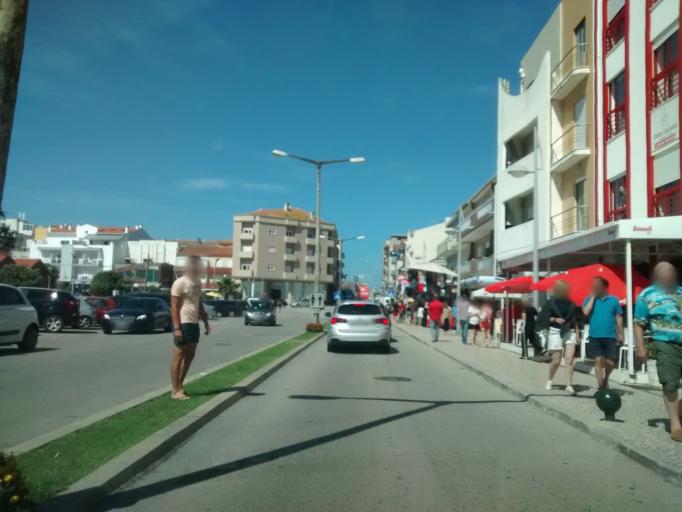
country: PT
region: Coimbra
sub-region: Mira
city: Mira
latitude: 40.4557
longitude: -8.8003
